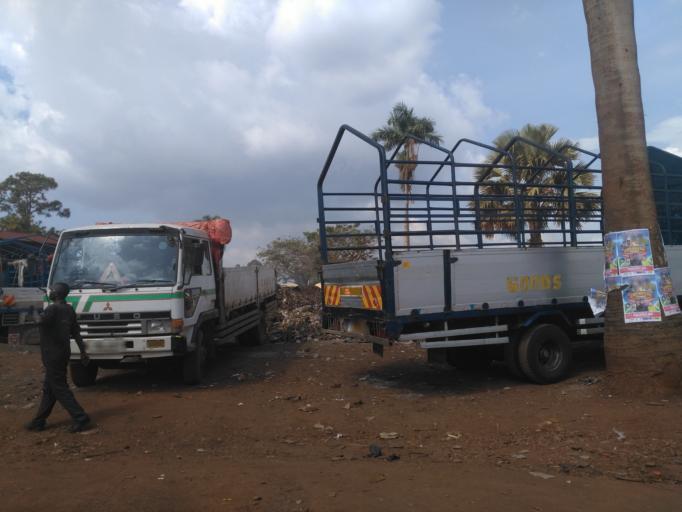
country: UG
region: Eastern Region
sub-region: Jinja District
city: Jinja
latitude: 0.4287
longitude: 33.2152
